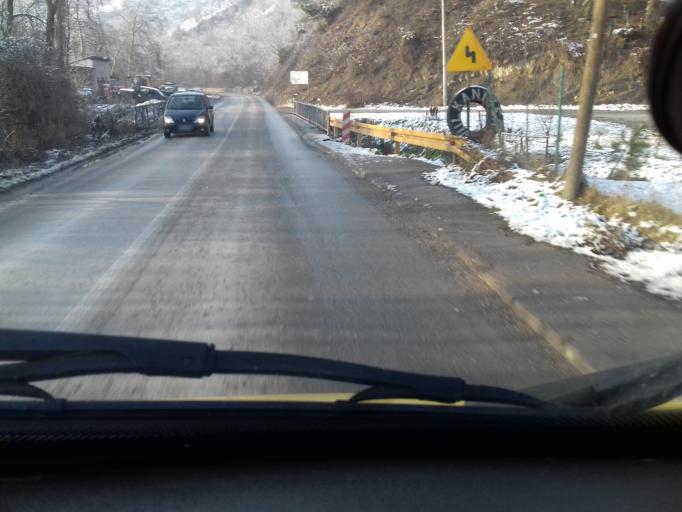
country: BA
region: Federation of Bosnia and Herzegovina
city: Visoko
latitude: 43.9978
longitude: 18.2159
